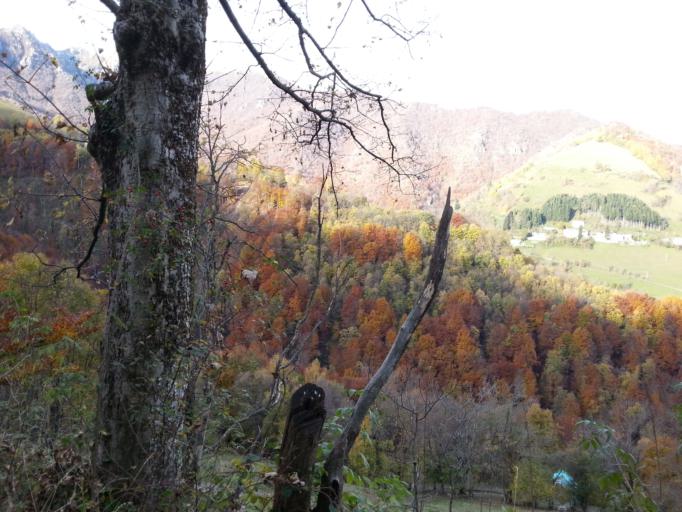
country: IT
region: Lombardy
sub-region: Provincia di Lecco
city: Morterone
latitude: 45.8764
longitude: 9.4967
